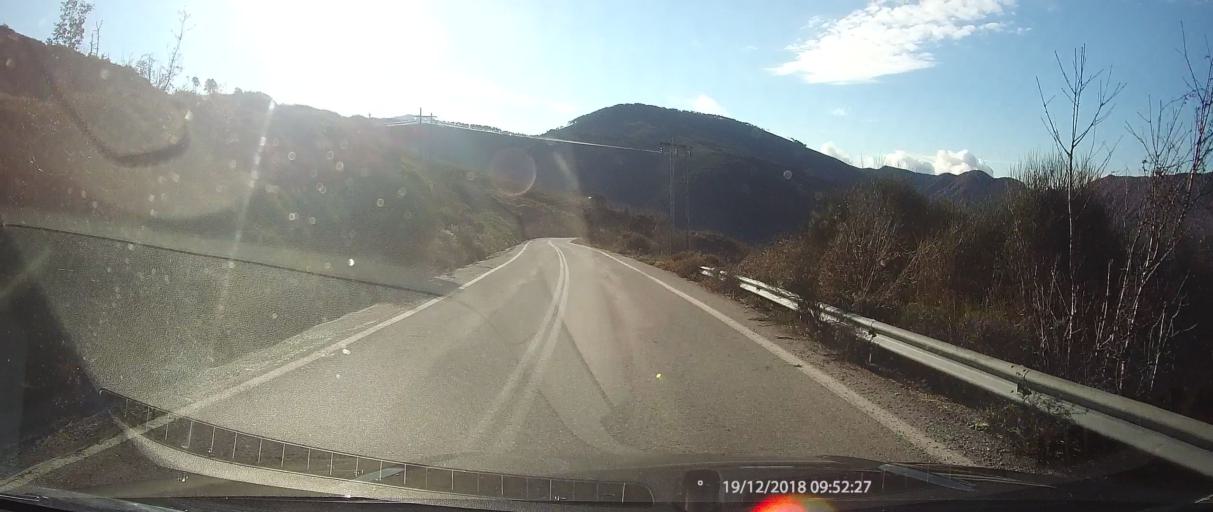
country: GR
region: Peloponnese
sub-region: Nomos Messinias
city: Paralia Vergas
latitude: 37.0745
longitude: 22.2543
